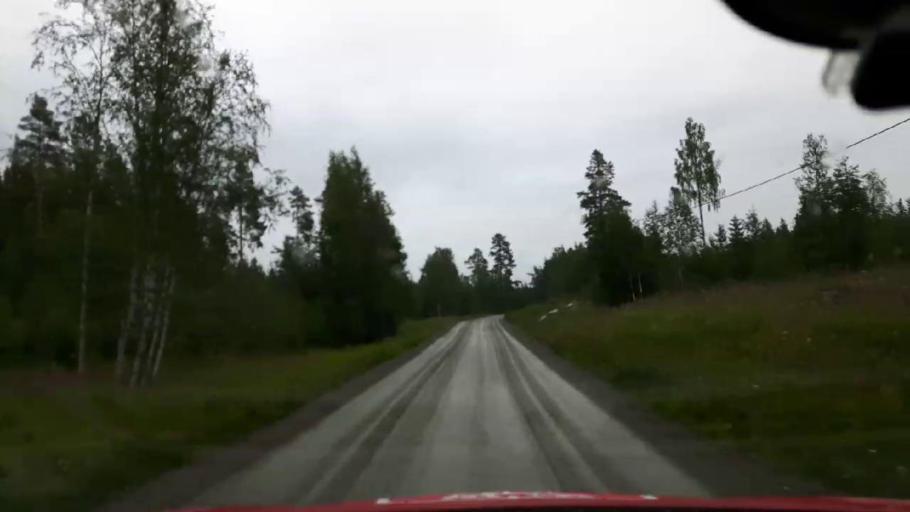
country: SE
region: Jaemtland
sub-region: OEstersunds Kommun
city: Brunflo
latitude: 62.8822
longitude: 14.8780
